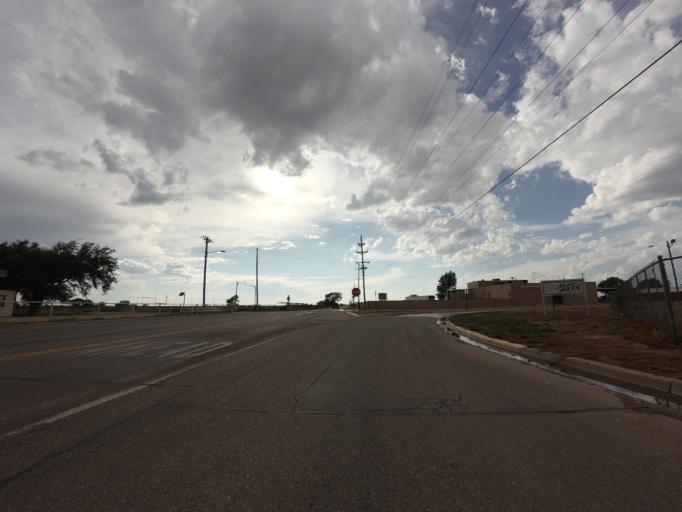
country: US
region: New Mexico
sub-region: Curry County
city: Clovis
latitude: 34.3902
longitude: -103.2197
